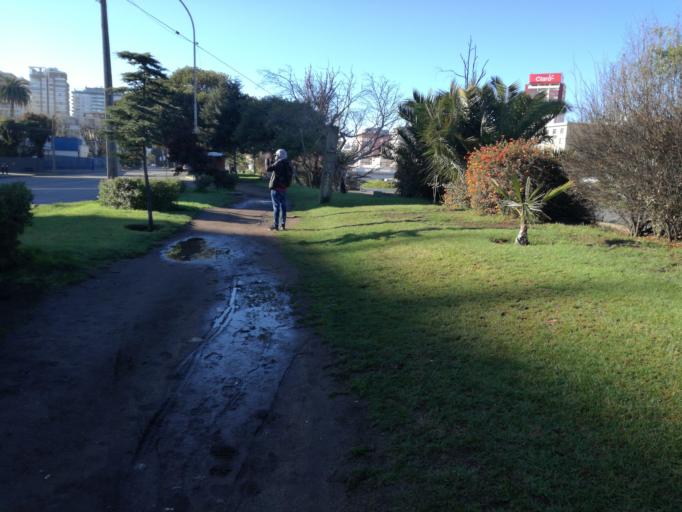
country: CL
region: Valparaiso
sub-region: Provincia de Valparaiso
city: Vina del Mar
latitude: -33.0214
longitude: -71.5579
